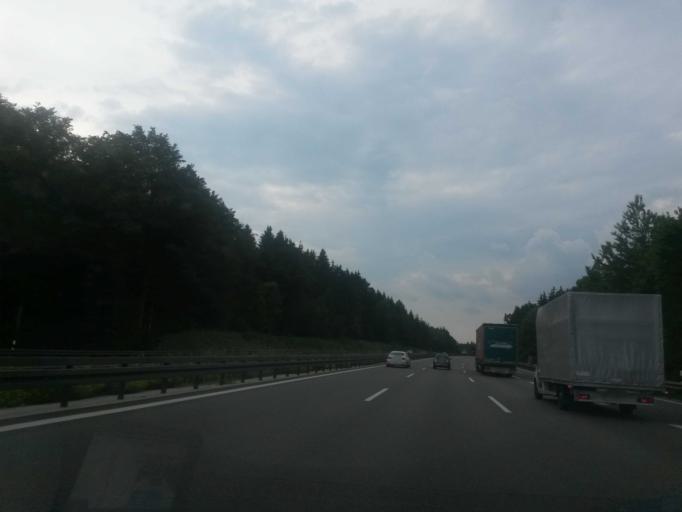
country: DE
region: Bavaria
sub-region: Upper Bavaria
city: Denkendorf
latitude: 48.9533
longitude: 11.4295
